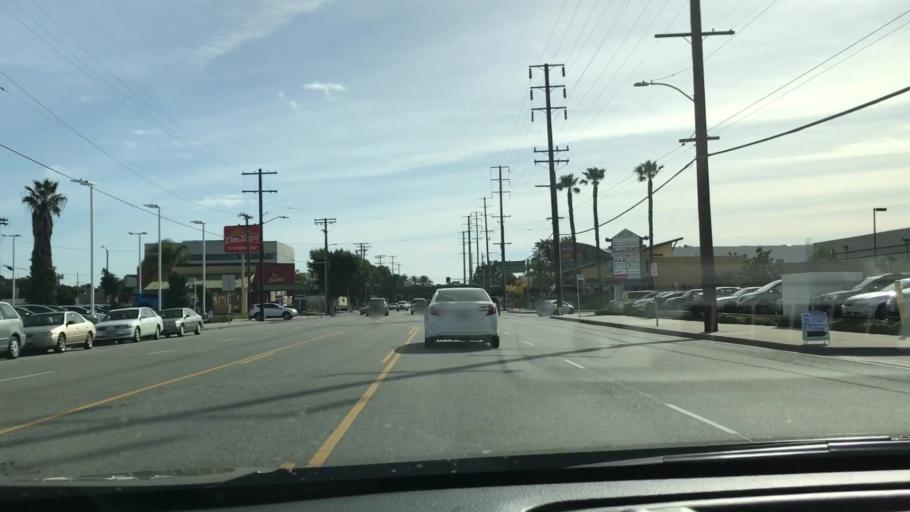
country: US
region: California
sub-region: Los Angeles County
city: Gardena
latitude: 33.8627
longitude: -118.3092
